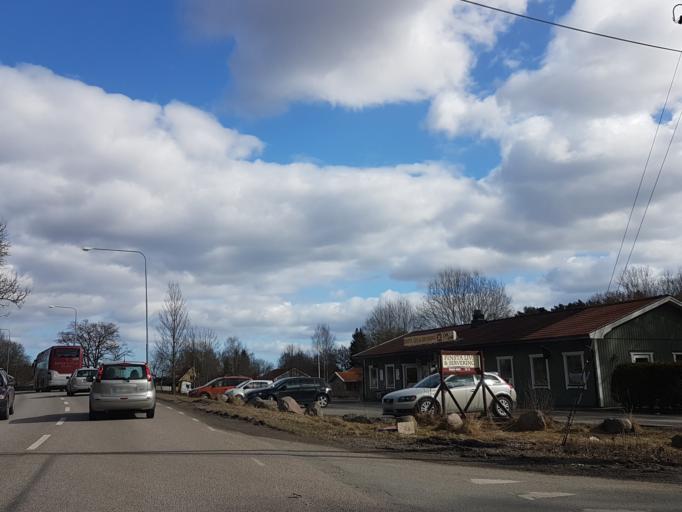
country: SE
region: Stockholm
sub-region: Norrtalje Kommun
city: Rimbo
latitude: 59.7369
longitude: 18.4937
